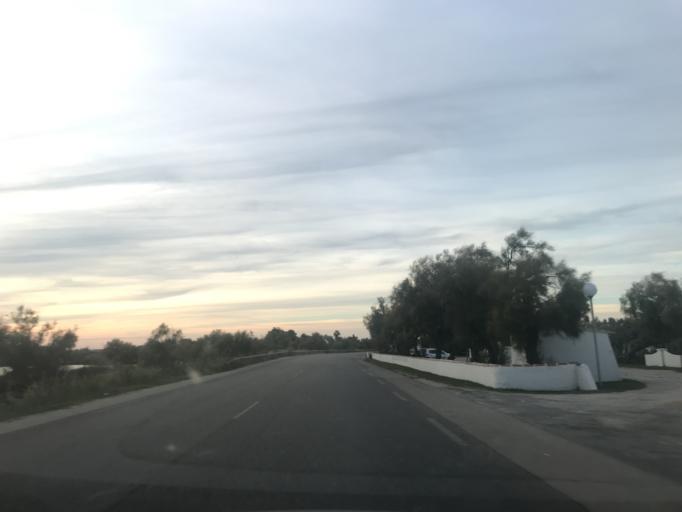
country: FR
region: Provence-Alpes-Cote d'Azur
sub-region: Departement des Bouches-du-Rhone
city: Saintes-Maries-de-la-Mer
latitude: 43.4630
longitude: 4.4201
